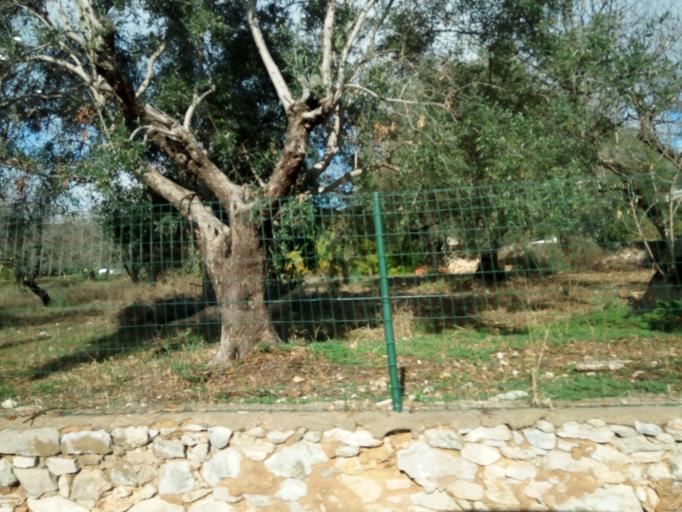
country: PT
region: Faro
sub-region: Faro
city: Santa Barbara de Nexe
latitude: 37.1115
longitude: -7.9618
